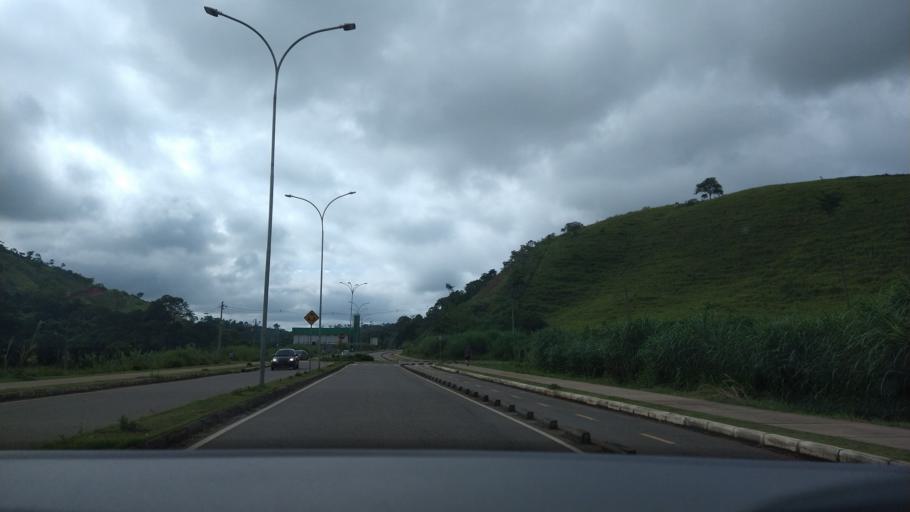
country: BR
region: Minas Gerais
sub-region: Vicosa
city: Vicosa
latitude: -20.7709
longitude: -42.8574
